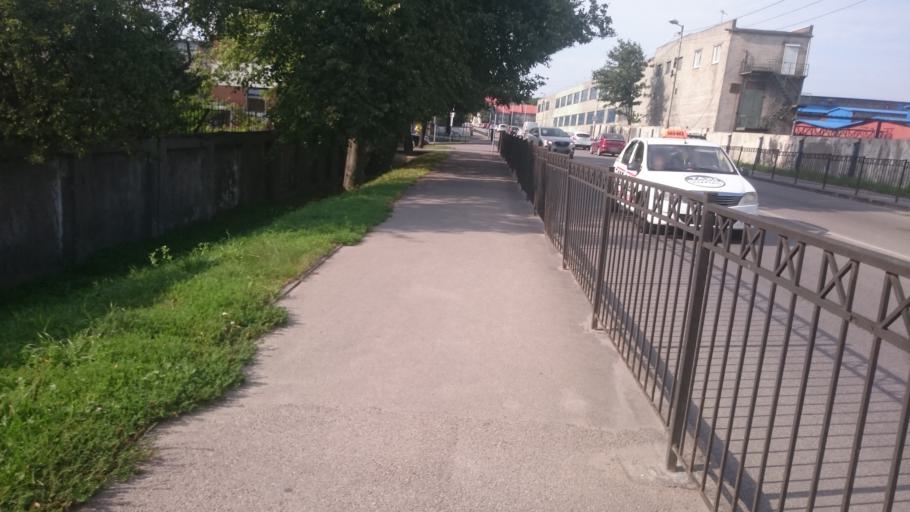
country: RU
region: Kaliningrad
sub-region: Gorod Kaliningrad
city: Kaliningrad
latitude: 54.7079
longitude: 20.4588
